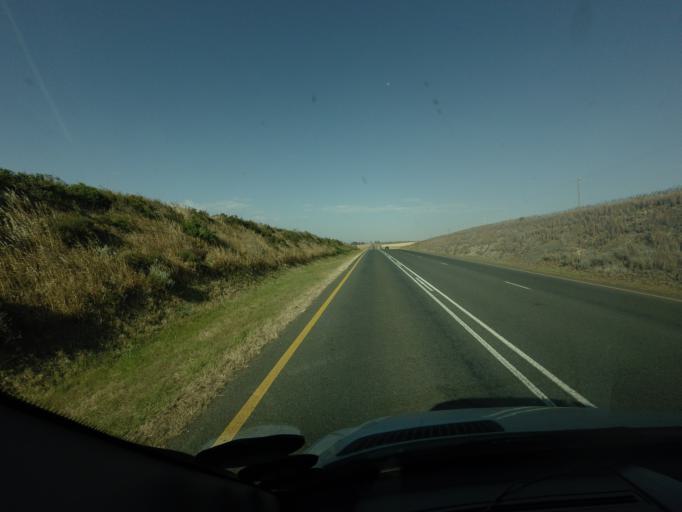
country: ZA
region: Western Cape
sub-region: Cape Winelands District Municipality
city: Ashton
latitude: -34.1560
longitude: 19.8791
